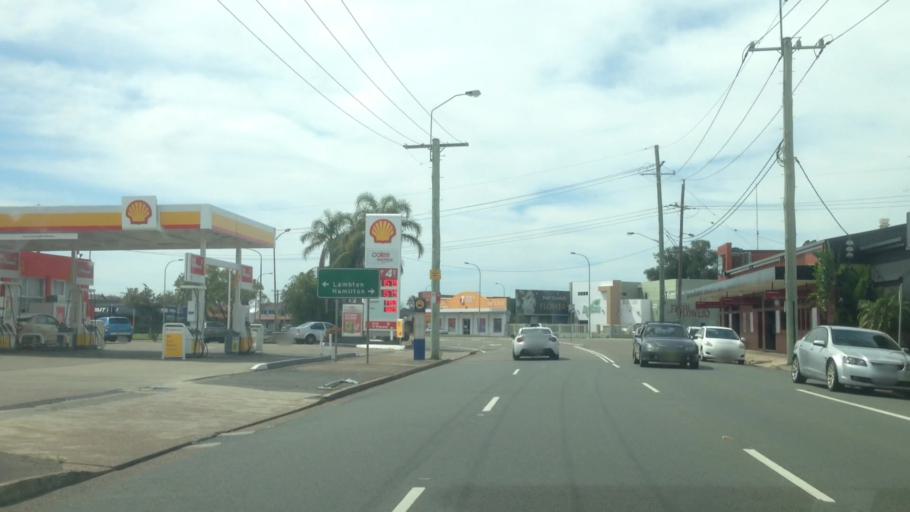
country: AU
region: New South Wales
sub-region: Newcastle
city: Broadmeadow
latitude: -32.9255
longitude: 151.7363
